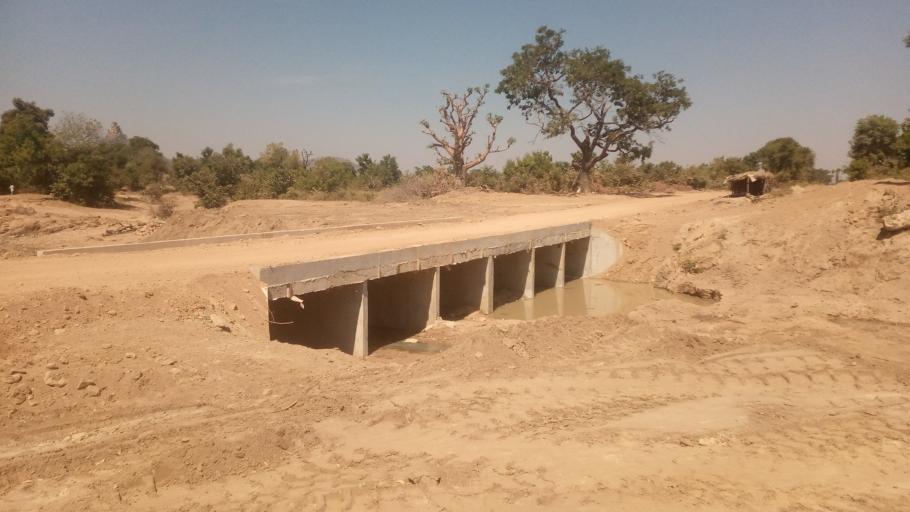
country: NG
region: Adamawa
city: Yola
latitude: 9.0771
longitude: 12.3833
